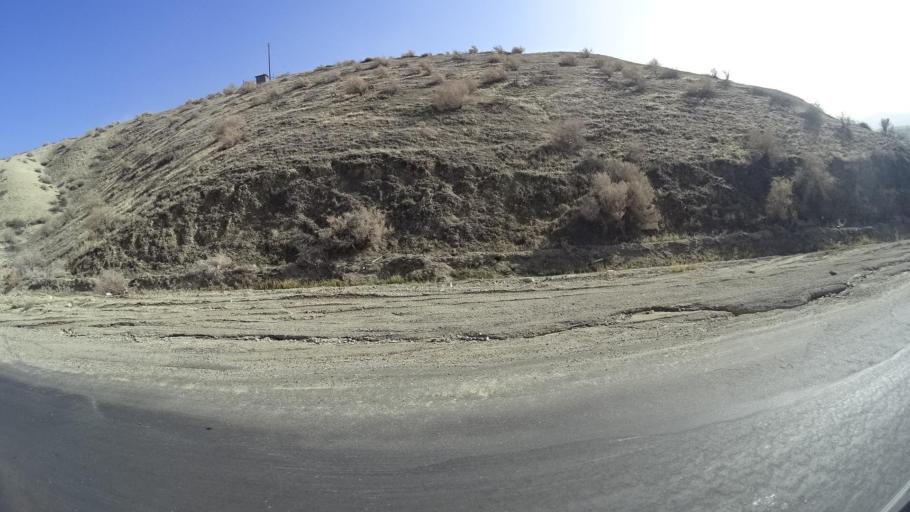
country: US
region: California
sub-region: Kern County
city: Maricopa
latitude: 35.0405
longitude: -119.4292
